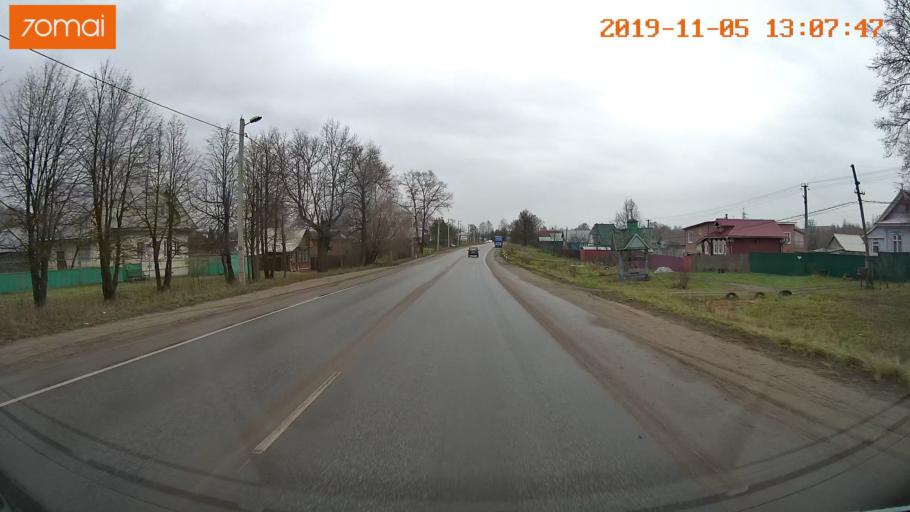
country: RU
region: Ivanovo
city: Kitovo
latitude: 56.8662
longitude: 41.2848
